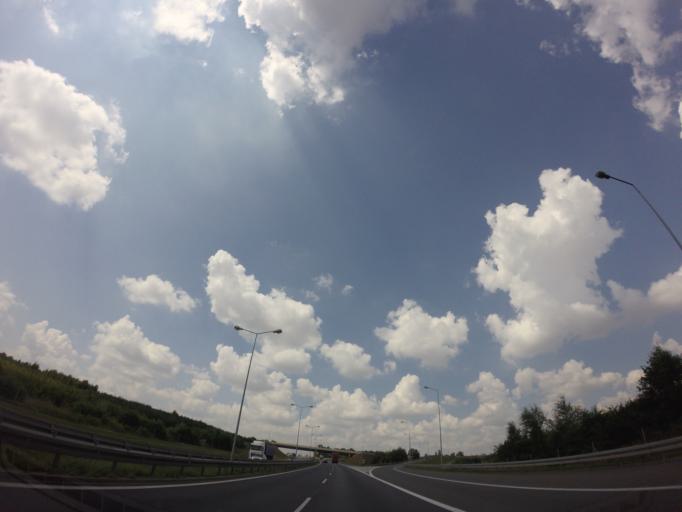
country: PL
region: Opole Voivodeship
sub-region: Powiat strzelecki
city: Ujazd
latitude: 50.4452
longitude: 18.3510
